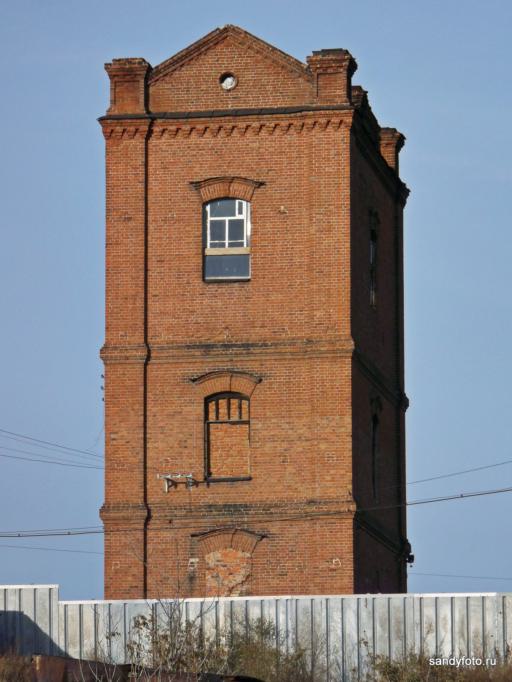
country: RU
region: Chelyabinsk
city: Troitsk
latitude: 54.0783
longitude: 61.5901
